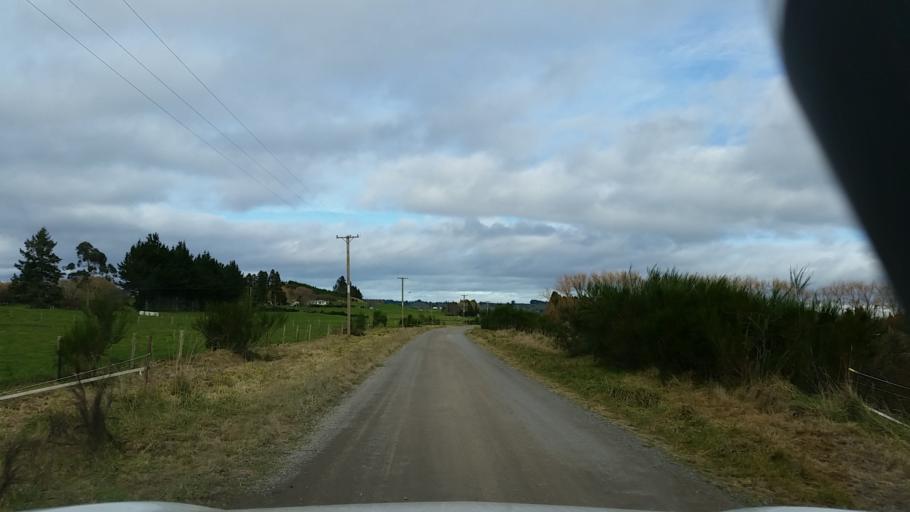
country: NZ
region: Bay of Plenty
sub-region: Whakatane District
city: Murupara
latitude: -38.2880
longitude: 176.5475
